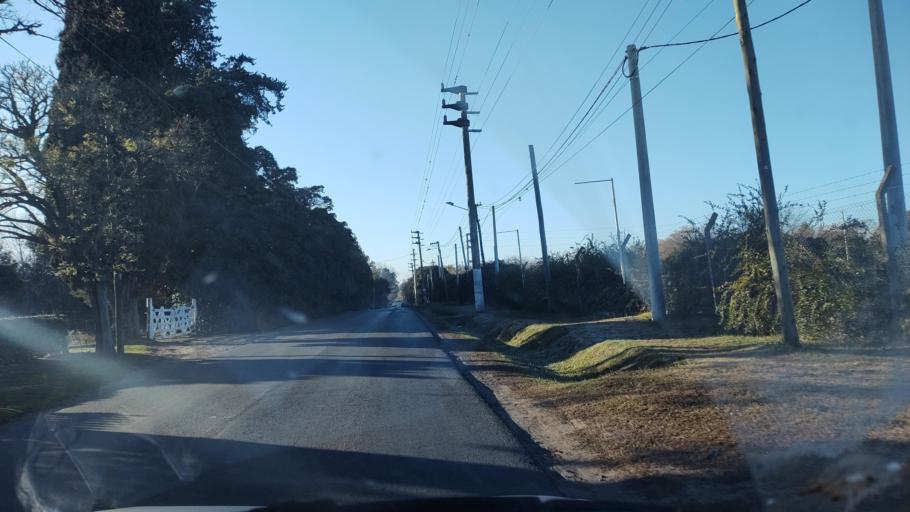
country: AR
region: Buenos Aires
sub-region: Partido de La Plata
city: La Plata
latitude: -34.8994
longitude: -58.0650
